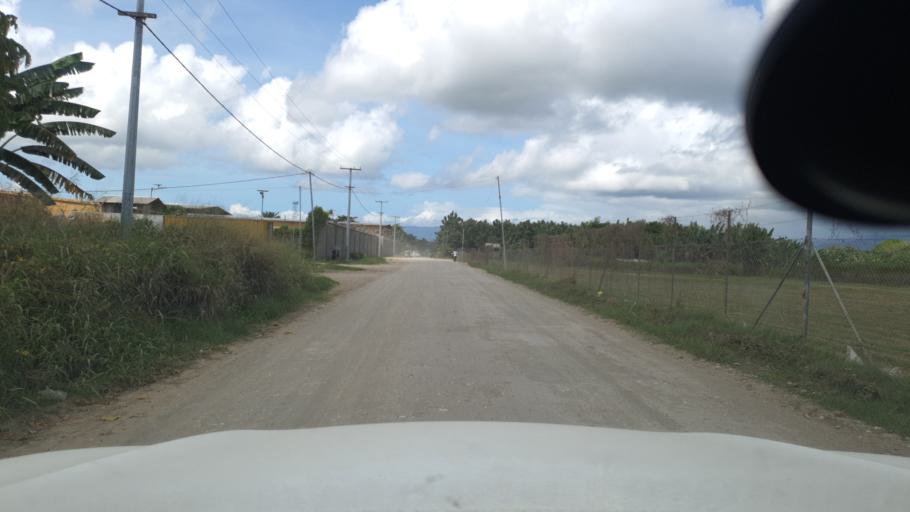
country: SB
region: Guadalcanal
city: Honiara
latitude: -9.4237
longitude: 160.0372
